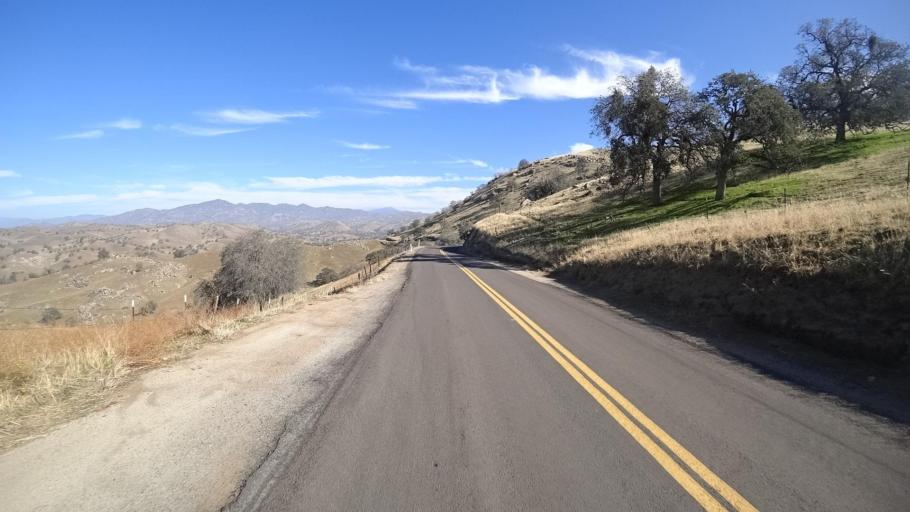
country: US
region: California
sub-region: Tulare County
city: Richgrove
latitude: 35.6932
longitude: -118.8681
